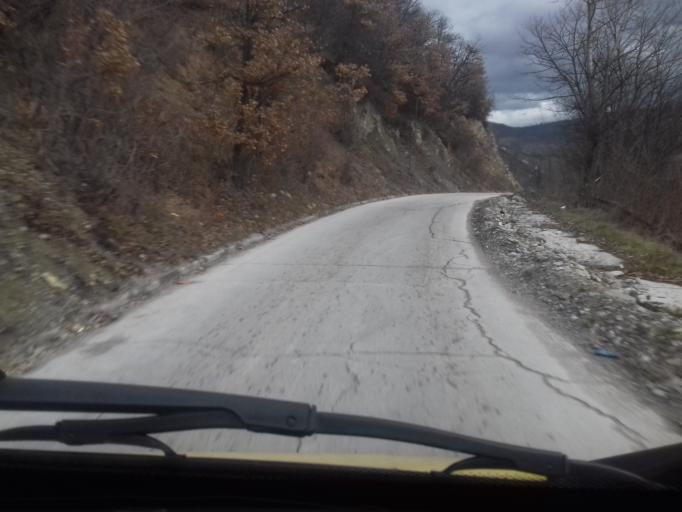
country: BA
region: Federation of Bosnia and Herzegovina
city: Zenica
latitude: 44.2228
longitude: 17.9670
